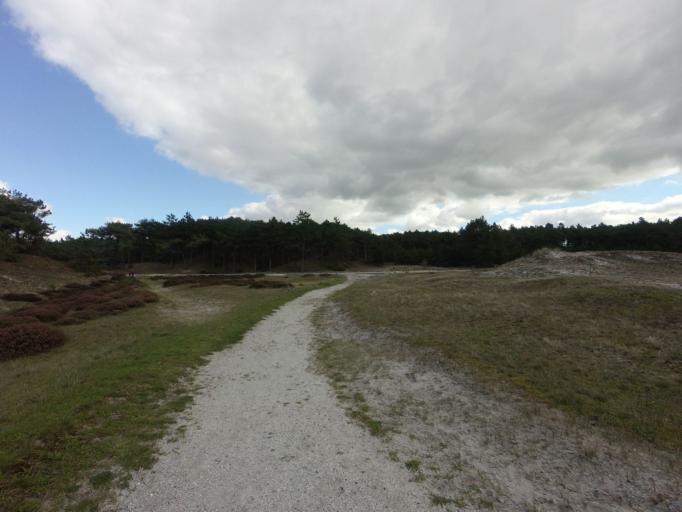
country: NL
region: North Holland
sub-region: Gemeente Bergen
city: Egmond aan Zee
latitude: 52.7113
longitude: 4.6636
